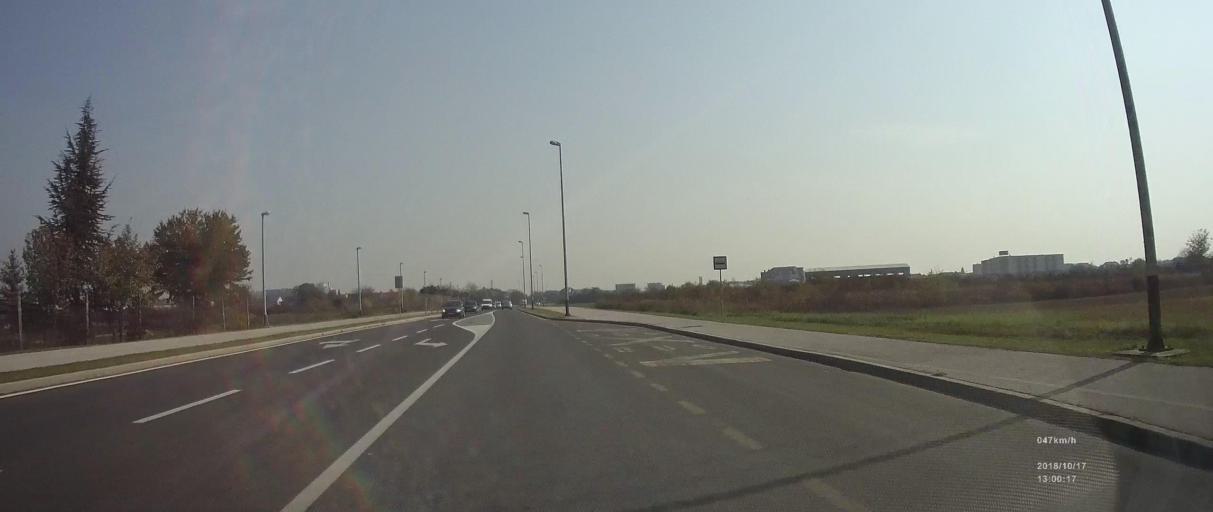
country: HR
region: Zagrebacka
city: Gradici
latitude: 45.7158
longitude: 16.0521
